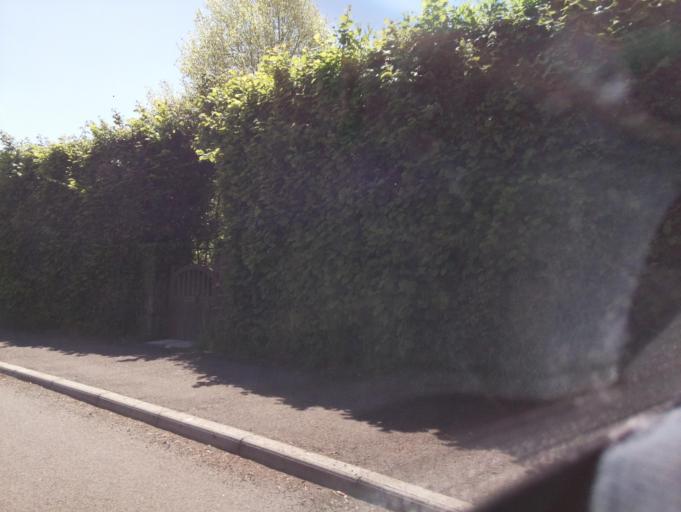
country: GB
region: Wales
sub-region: Monmouthshire
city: Caldicot
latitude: 51.6411
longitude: -2.7549
